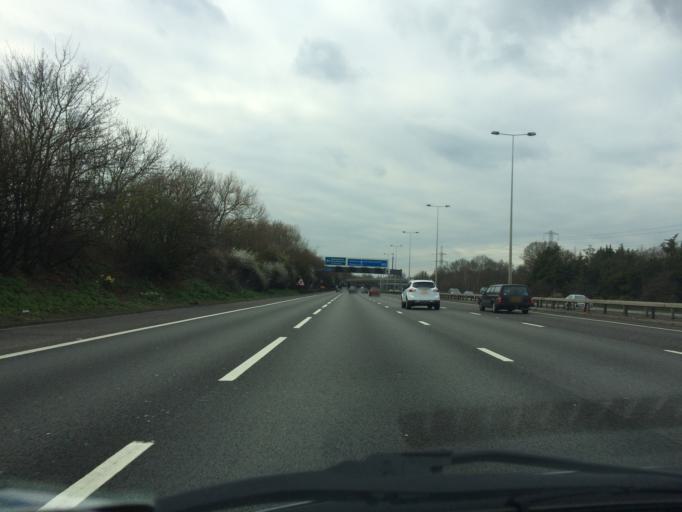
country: GB
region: England
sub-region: Surrey
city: Chertsey
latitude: 51.3872
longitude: -0.5240
